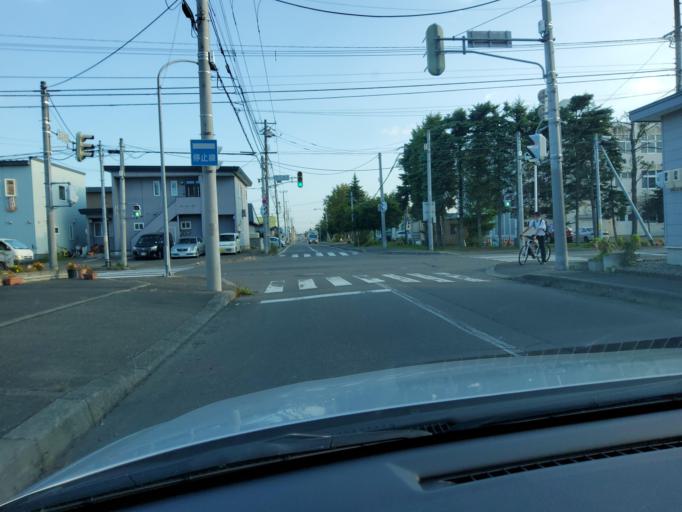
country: JP
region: Hokkaido
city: Obihiro
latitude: 42.9408
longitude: 143.1824
